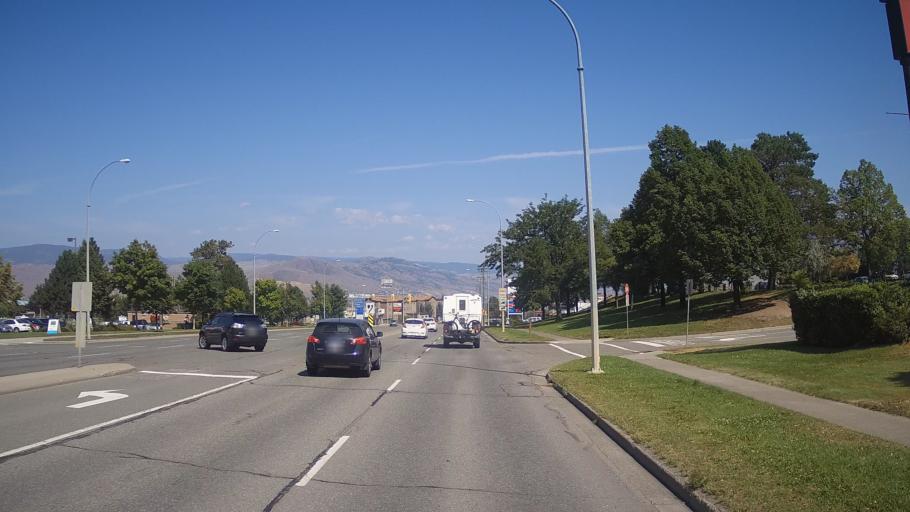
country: CA
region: British Columbia
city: Kamloops
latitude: 50.6681
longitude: -120.3542
